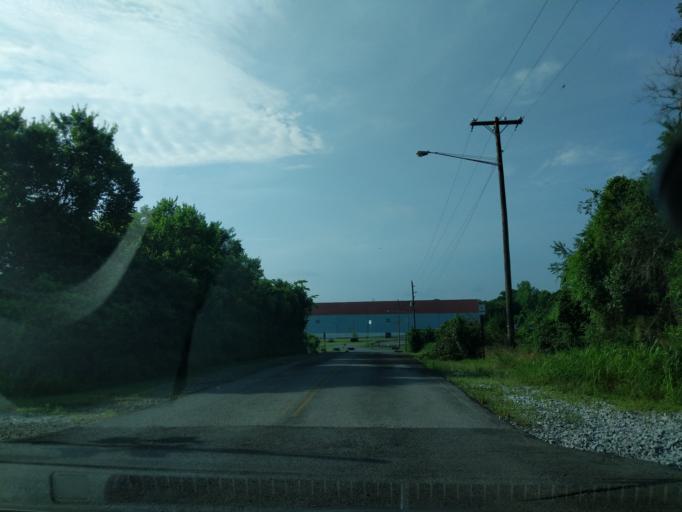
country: US
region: Tennessee
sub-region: Sumner County
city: Hendersonville
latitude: 36.3041
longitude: -86.6645
